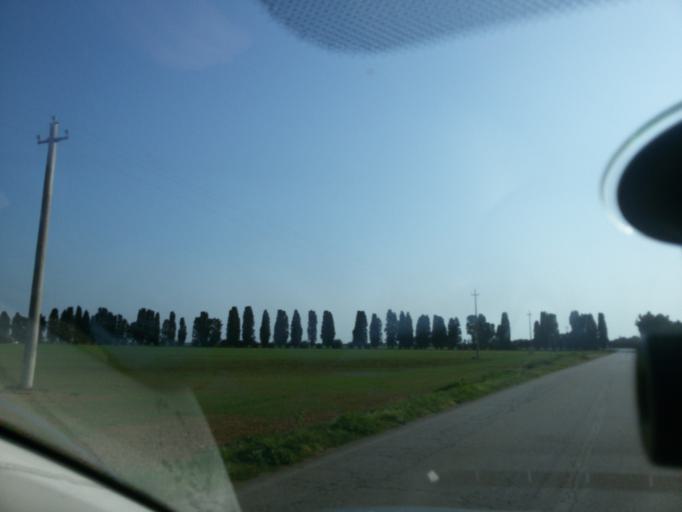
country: IT
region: Apulia
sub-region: Provincia di Brindisi
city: Mesagne
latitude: 40.5977
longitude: 17.8166
